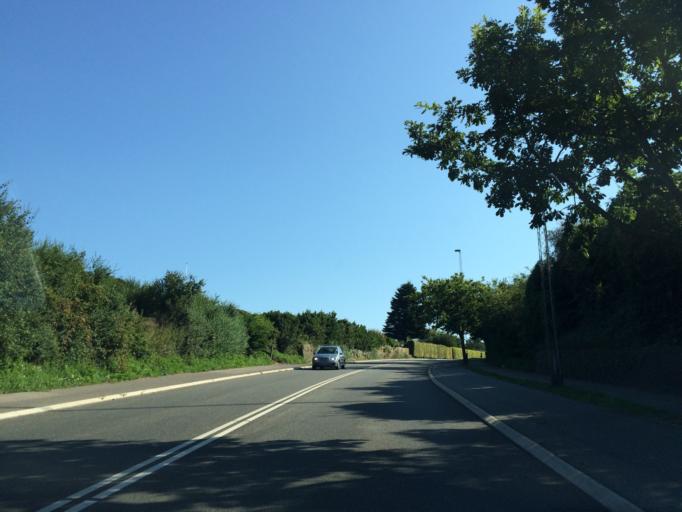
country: DK
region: South Denmark
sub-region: Kolding Kommune
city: Kolding
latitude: 55.5022
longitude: 9.5213
